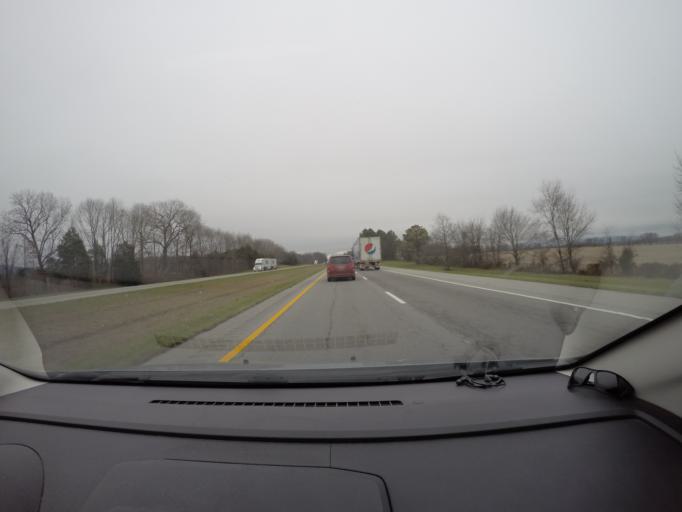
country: US
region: Tennessee
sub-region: Franklin County
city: Sewanee
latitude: 35.3438
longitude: -85.9432
